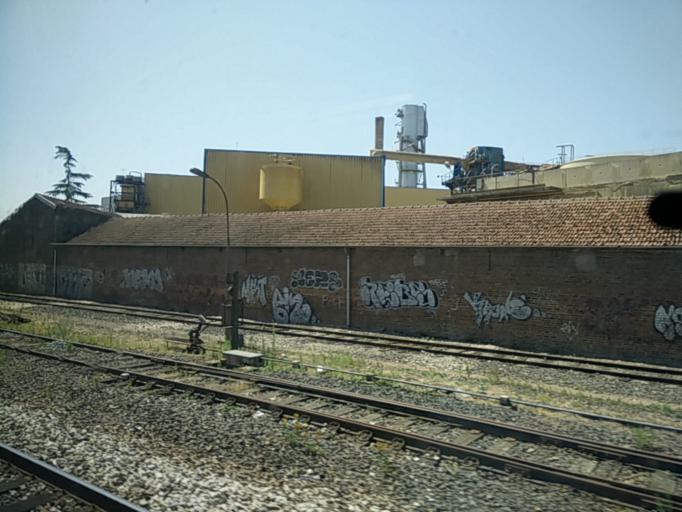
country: FR
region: Ile-de-France
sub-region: Departement de Seine-et-Marne
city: Nangis
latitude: 48.5635
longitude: 3.0099
